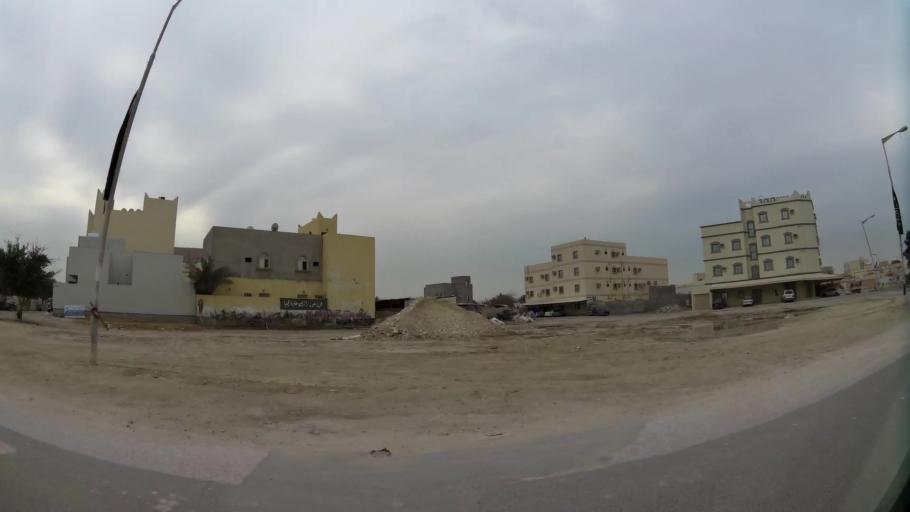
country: BH
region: Northern
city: Sitrah
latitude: 26.1435
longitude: 50.6089
